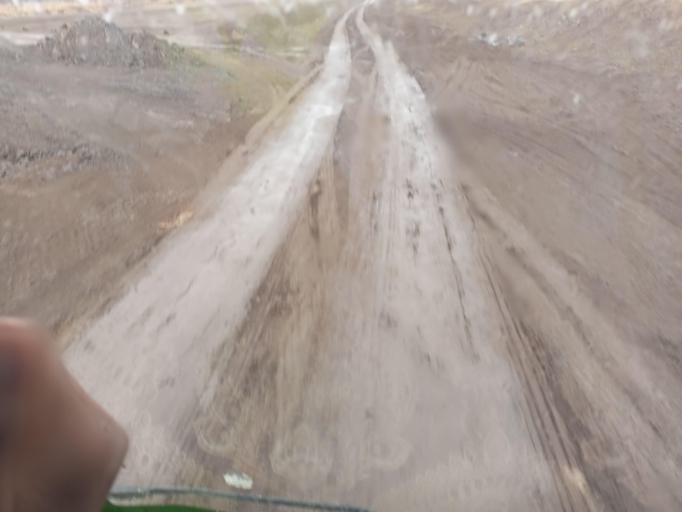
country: ET
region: Oromiya
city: Ziway
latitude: 7.7598
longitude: 38.6102
